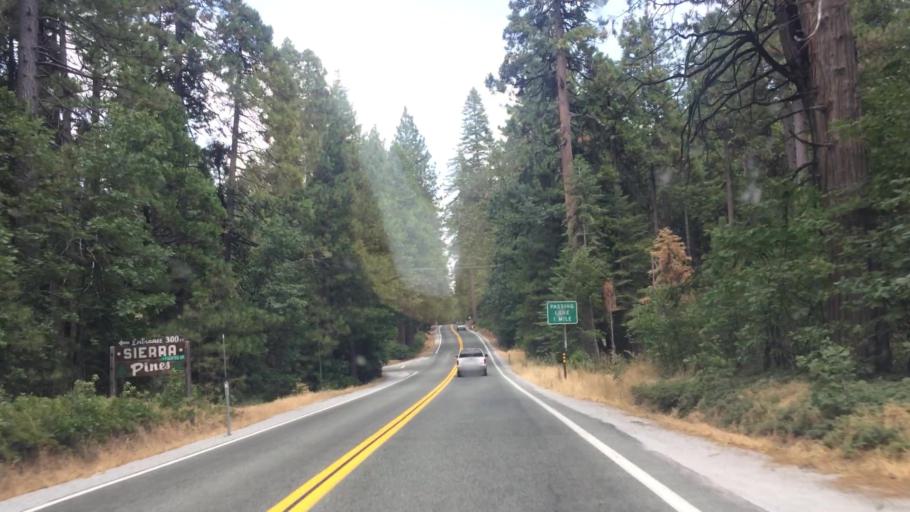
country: US
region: California
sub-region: Amador County
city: Pioneer
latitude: 38.5029
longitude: -120.4988
